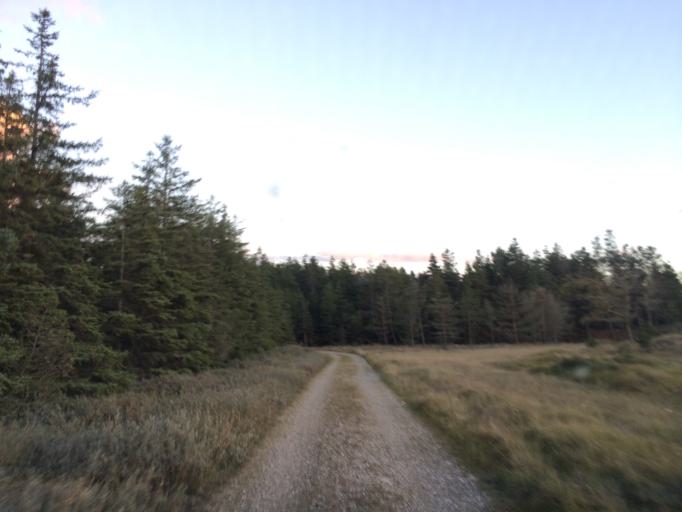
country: DK
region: Central Jutland
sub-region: Holstebro Kommune
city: Ulfborg
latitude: 56.2978
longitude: 8.1509
